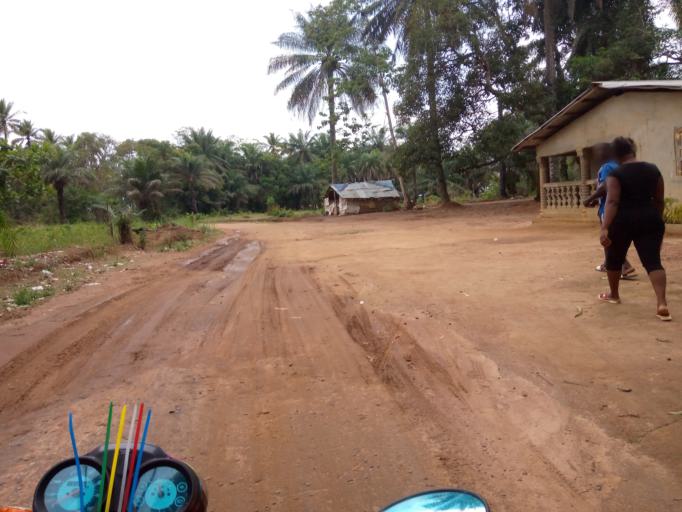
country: SL
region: Western Area
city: Waterloo
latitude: 8.3405
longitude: -13.0093
